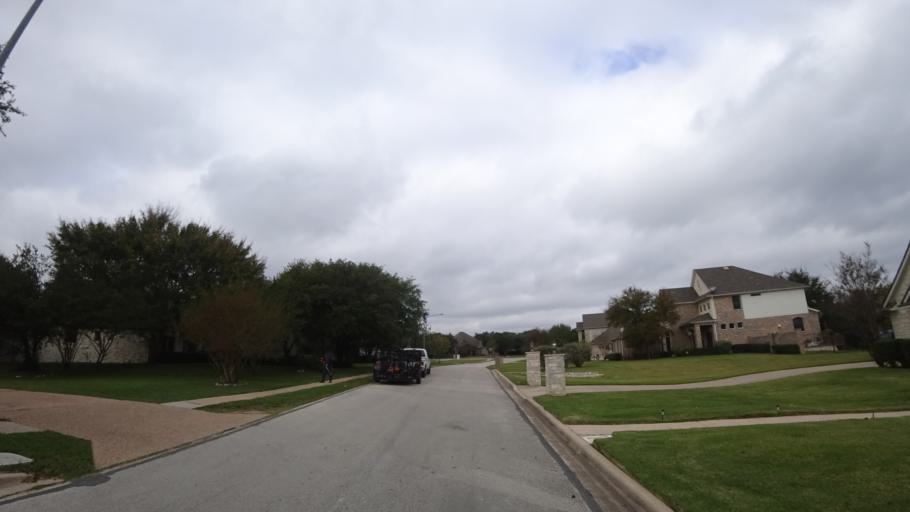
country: US
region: Texas
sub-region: Travis County
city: Barton Creek
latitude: 30.2561
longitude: -97.9068
